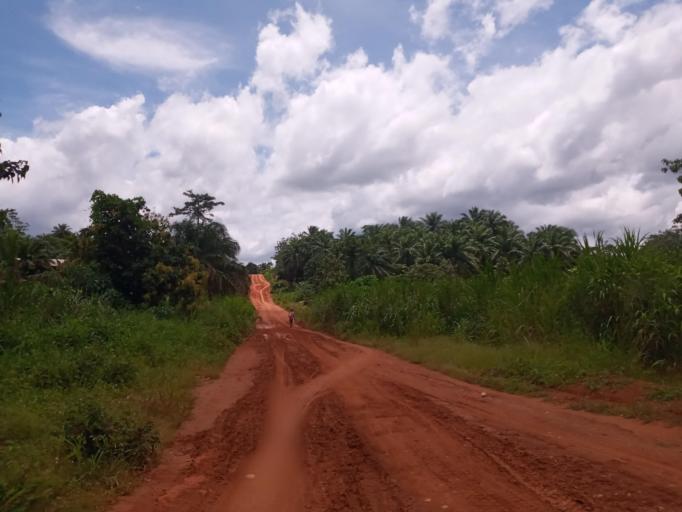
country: SL
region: Eastern Province
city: Koidu
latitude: 8.6444
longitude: -10.9117
